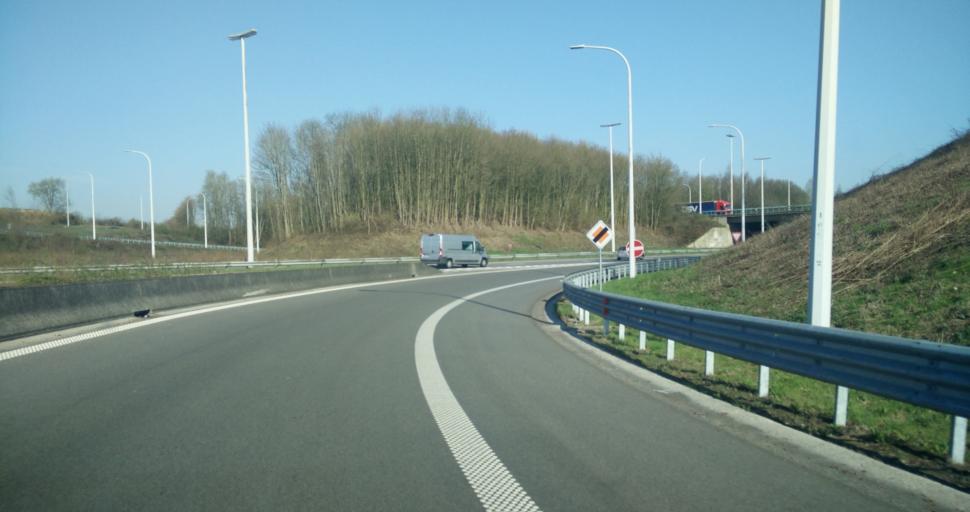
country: BE
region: Wallonia
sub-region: Province du Hainaut
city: Fleurus
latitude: 50.4696
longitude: 4.5010
